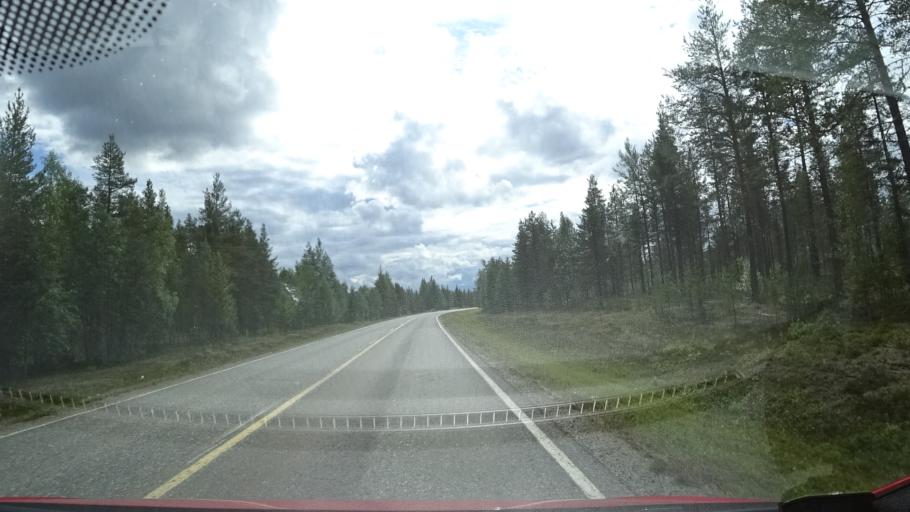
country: FI
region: Lapland
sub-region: Tunturi-Lappi
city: Kittilae
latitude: 67.5042
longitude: 24.8995
